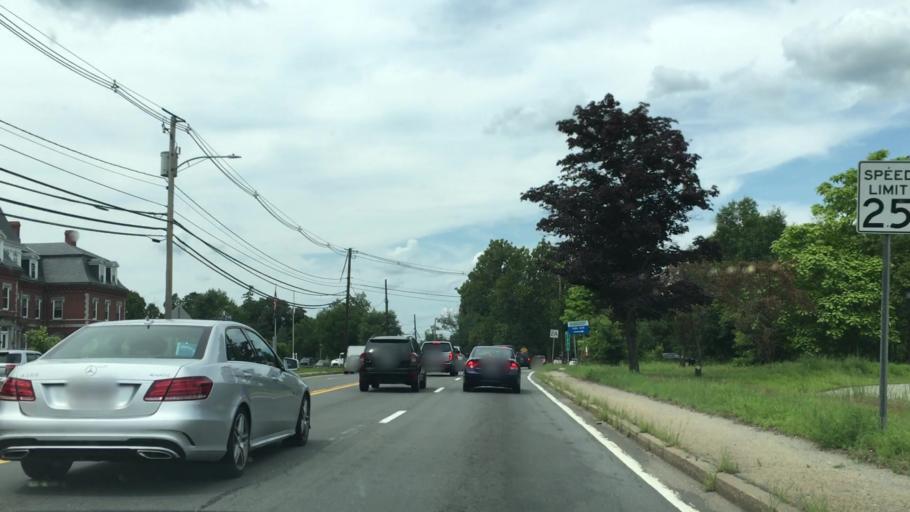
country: US
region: Massachusetts
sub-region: Middlesex County
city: West Concord
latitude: 42.4665
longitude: -71.3943
